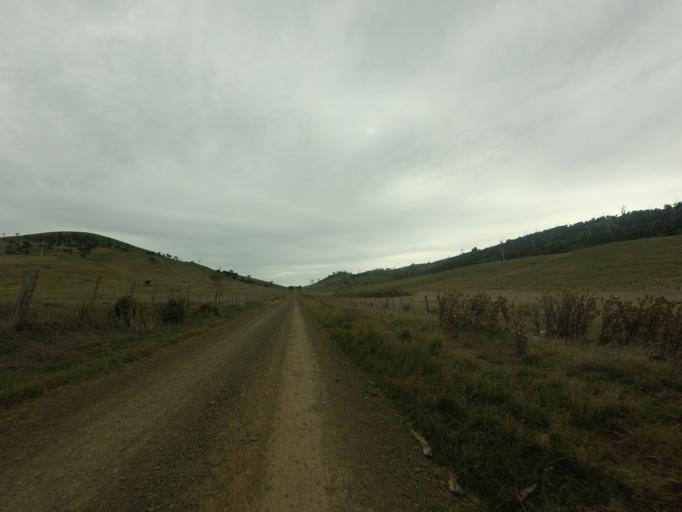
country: AU
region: Tasmania
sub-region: Derwent Valley
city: New Norfolk
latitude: -42.3800
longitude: 146.8673
